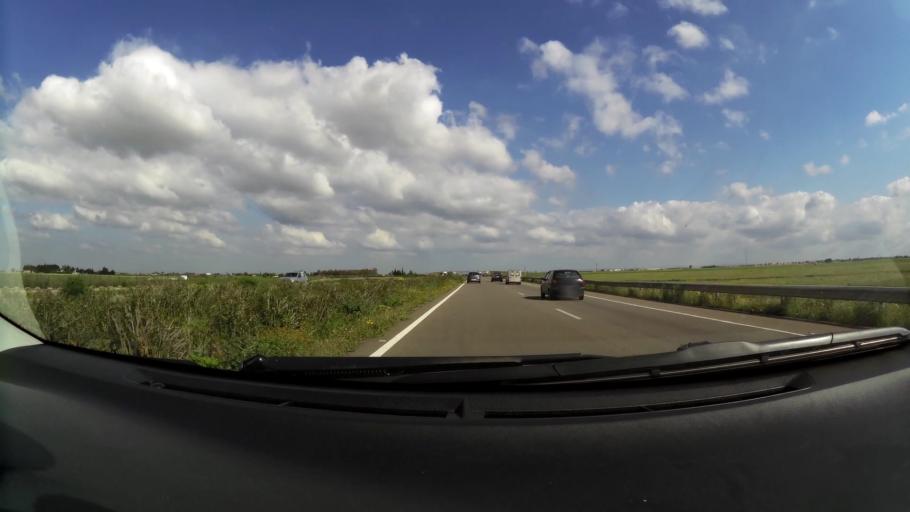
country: MA
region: Chaouia-Ouardigha
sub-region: Settat Province
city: Berrechid
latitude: 33.3106
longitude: -7.5919
